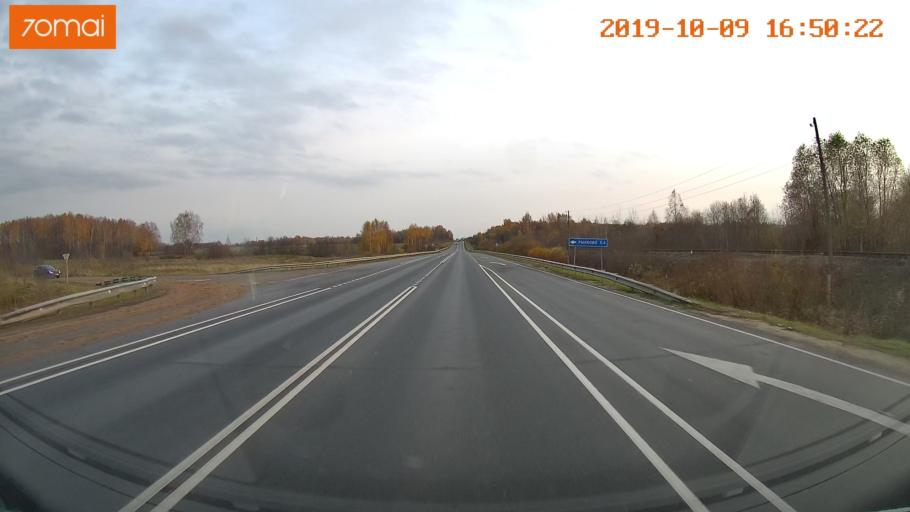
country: RU
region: Kostroma
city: Volgorechensk
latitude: 57.4018
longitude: 41.2081
